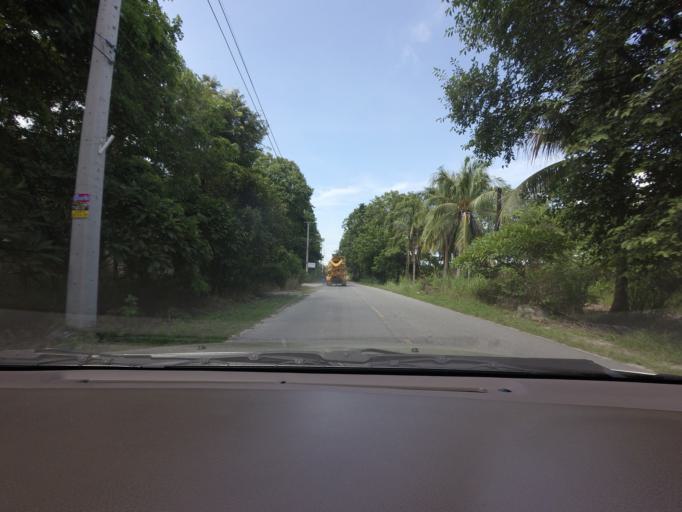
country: TH
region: Chon Buri
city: Chon Buri
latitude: 13.3179
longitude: 100.9977
